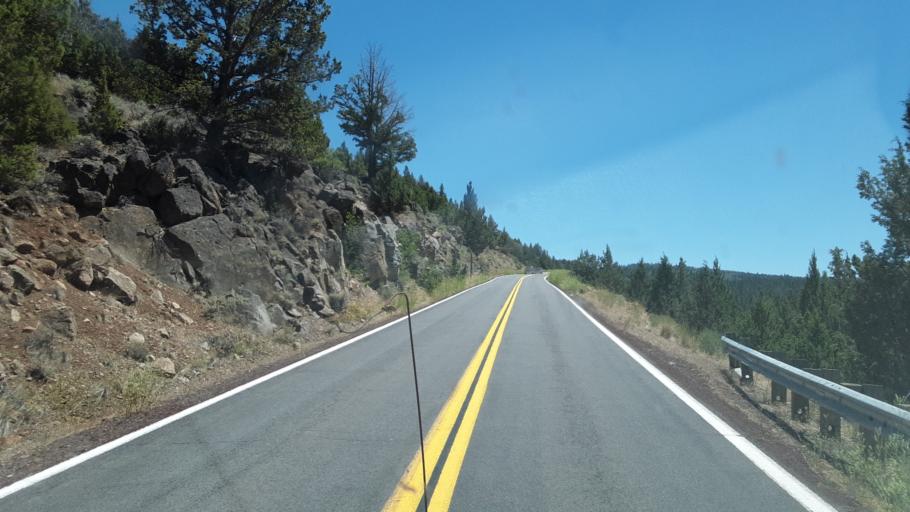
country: US
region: California
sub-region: Lassen County
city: Susanville
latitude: 40.6546
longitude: -120.6585
